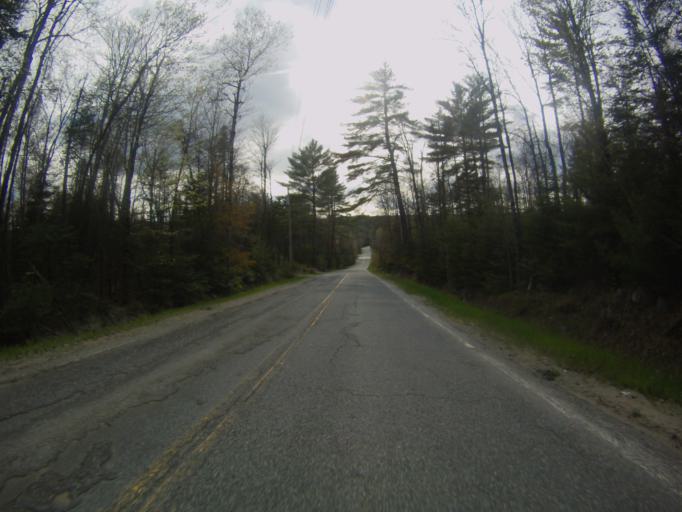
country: US
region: New York
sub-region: Warren County
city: Warrensburg
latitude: 43.8398
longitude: -73.8503
